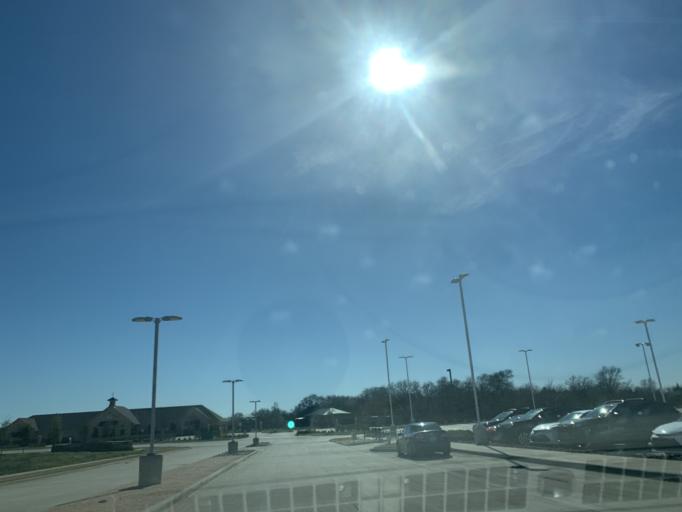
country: US
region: Texas
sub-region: Denton County
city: The Colony
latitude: 33.0810
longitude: -96.8469
